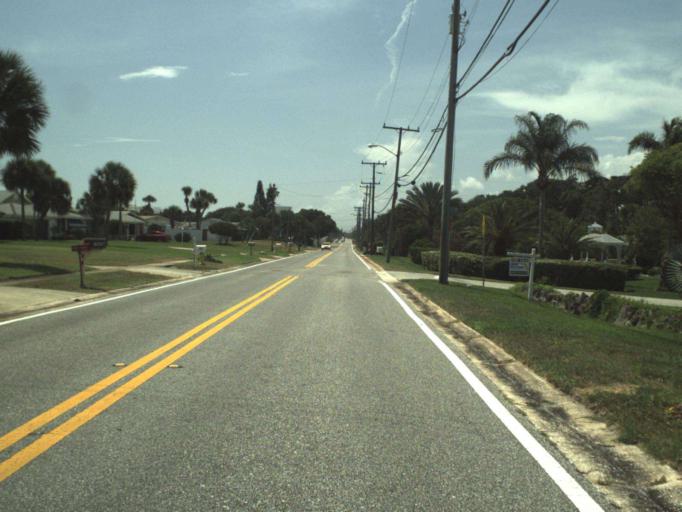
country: US
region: Florida
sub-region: Volusia County
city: Daytona Beach Shores
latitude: 29.1852
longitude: -80.9909
